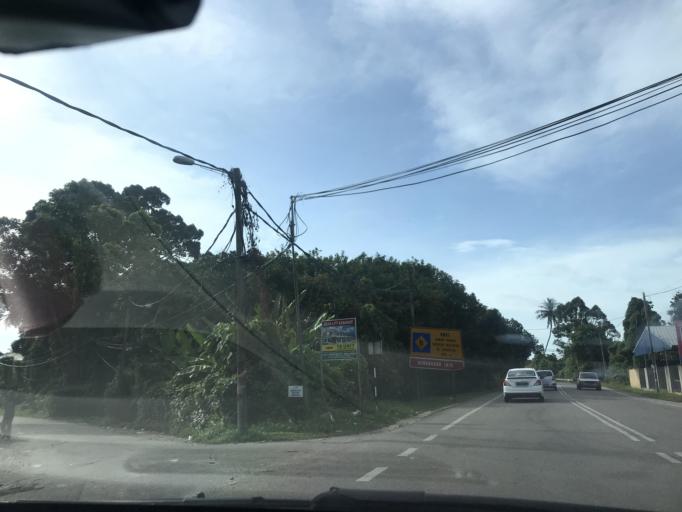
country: MY
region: Kelantan
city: Kota Bharu
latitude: 6.1277
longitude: 102.2021
